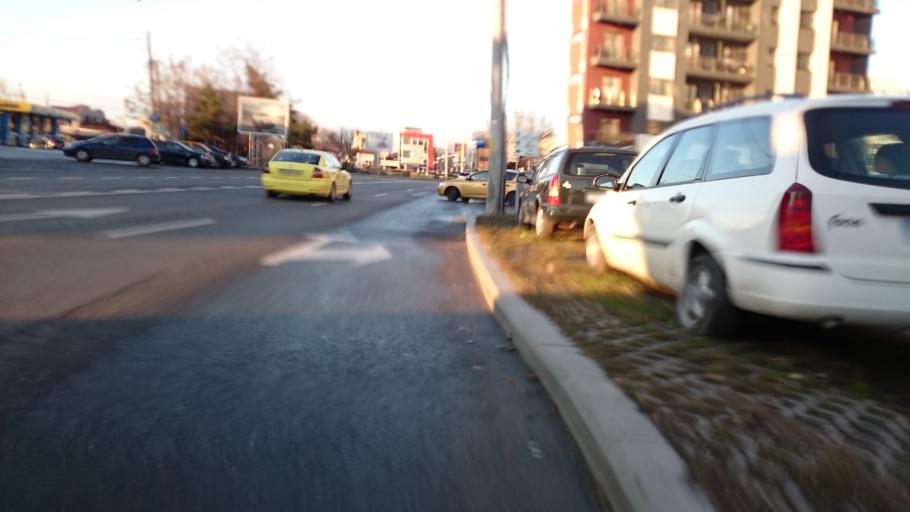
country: RO
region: Bucuresti
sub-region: Municipiul Bucuresti
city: Bucuresti
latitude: 44.4170
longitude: 26.0590
